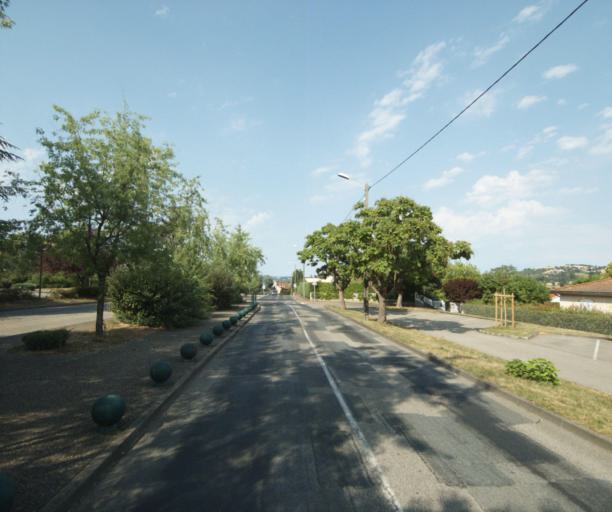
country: FR
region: Rhone-Alpes
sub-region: Departement du Rhone
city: Saint-Germain-Nuelles
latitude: 45.8314
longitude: 4.6078
